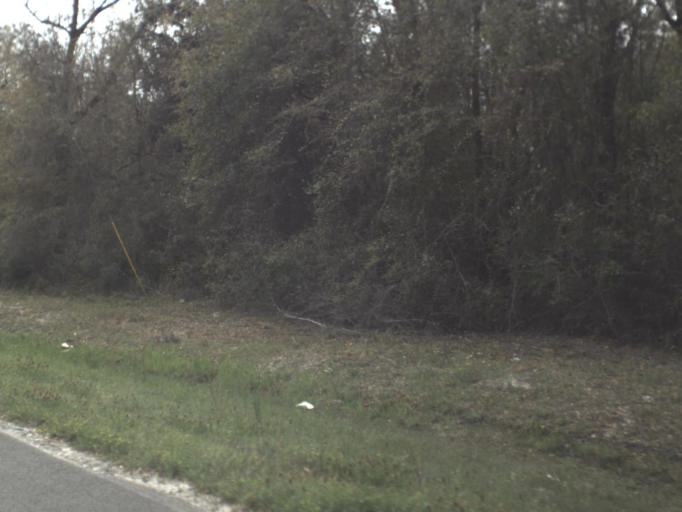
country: US
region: Florida
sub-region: Gulf County
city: Wewahitchka
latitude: 30.0647
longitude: -85.1917
